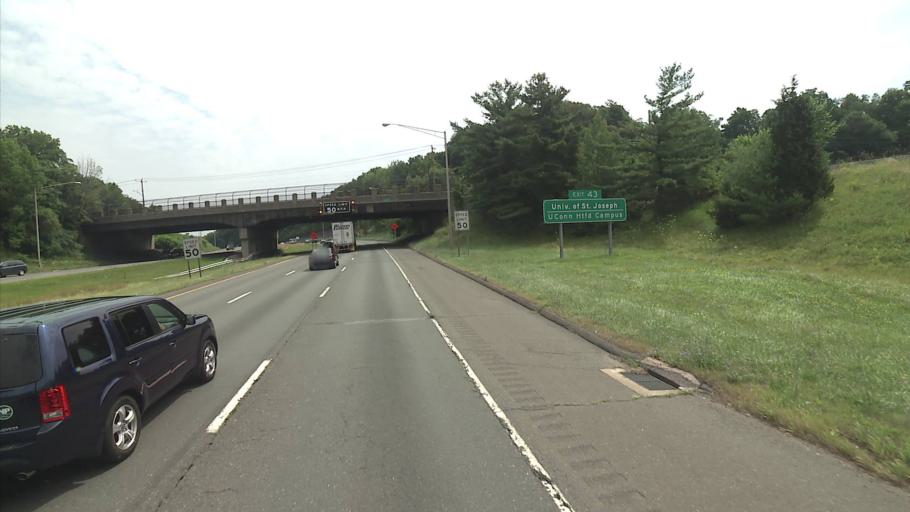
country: US
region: Connecticut
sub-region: Hartford County
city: West Hartford
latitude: 41.7349
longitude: -72.7439
